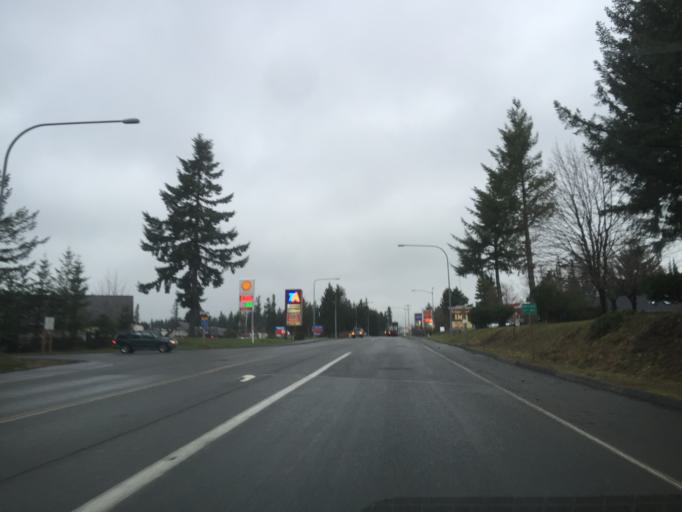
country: US
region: Washington
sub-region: King County
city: Tanner
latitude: 47.4667
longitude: -121.7161
